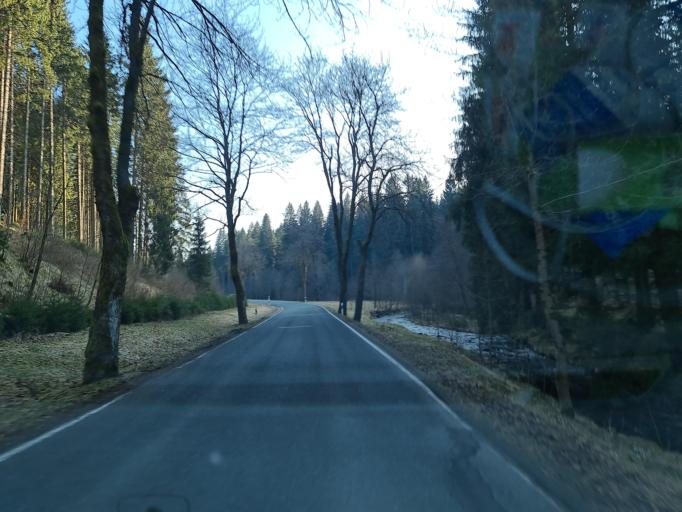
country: DE
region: Saxony
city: Schoenheide
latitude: 50.4715
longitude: 12.5233
